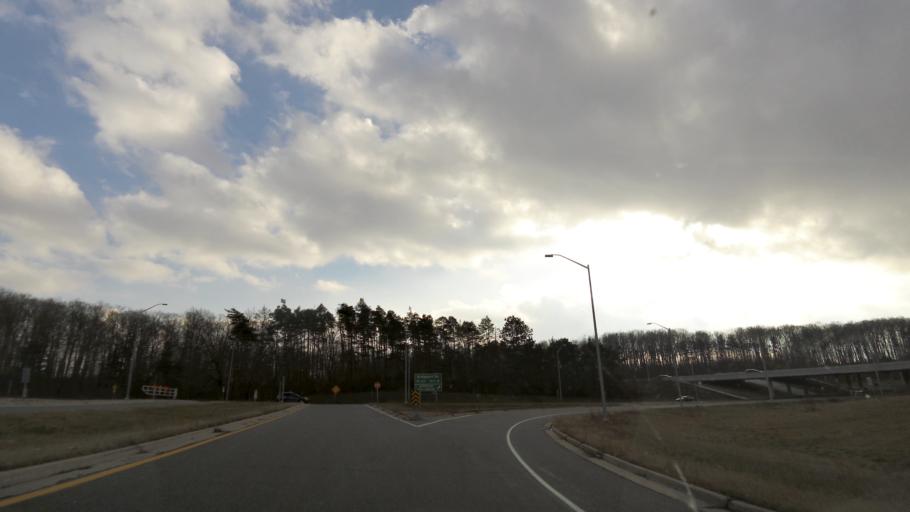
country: CA
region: Ontario
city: Waterloo
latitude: 43.4753
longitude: -80.4923
